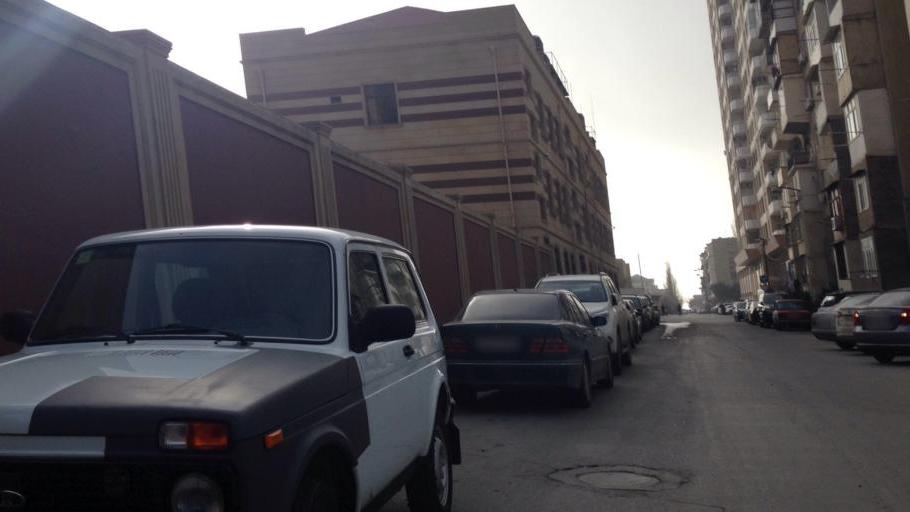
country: AZ
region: Baki
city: Baku
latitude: 40.3820
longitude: 49.8703
